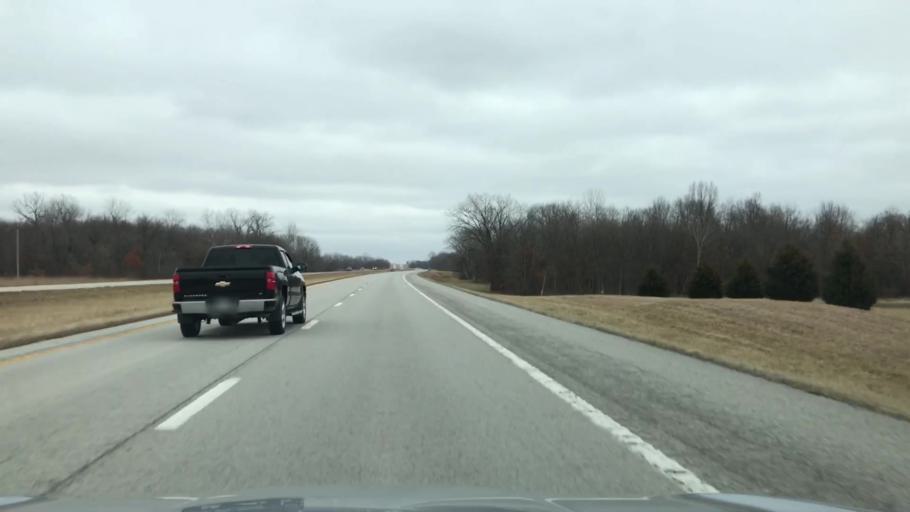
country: US
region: Missouri
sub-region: Livingston County
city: Chillicothe
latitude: 39.7767
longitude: -93.4408
